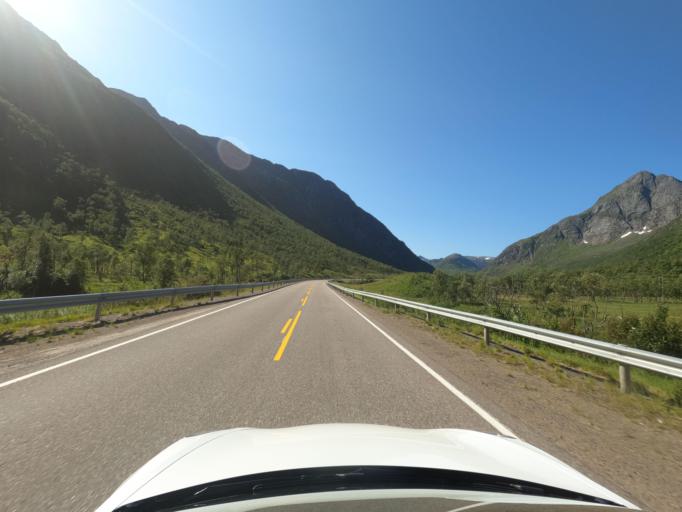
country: NO
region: Nordland
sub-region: Lodingen
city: Lodingen
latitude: 68.5125
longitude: 15.7358
